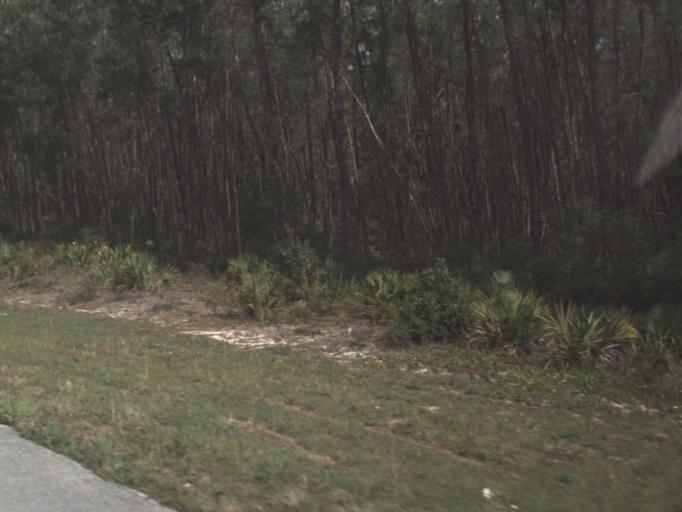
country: US
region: Florida
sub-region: Putnam County
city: Crescent City
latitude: 29.3200
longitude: -81.6985
